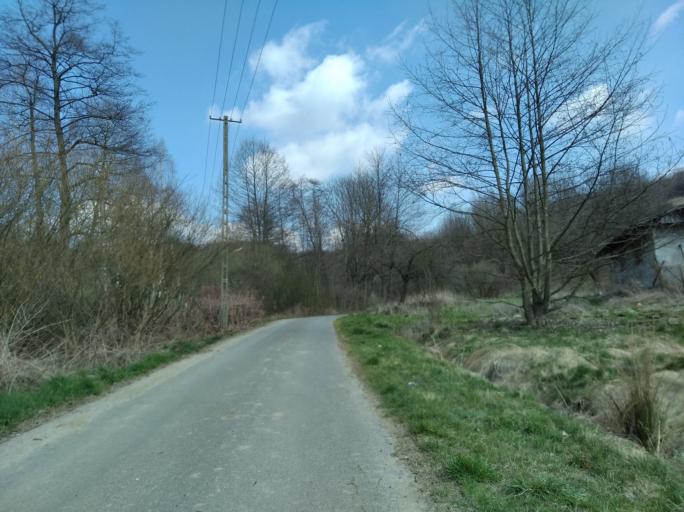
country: PL
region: Subcarpathian Voivodeship
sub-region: Powiat strzyzowski
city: Strzyzow
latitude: 49.8406
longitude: 21.8370
